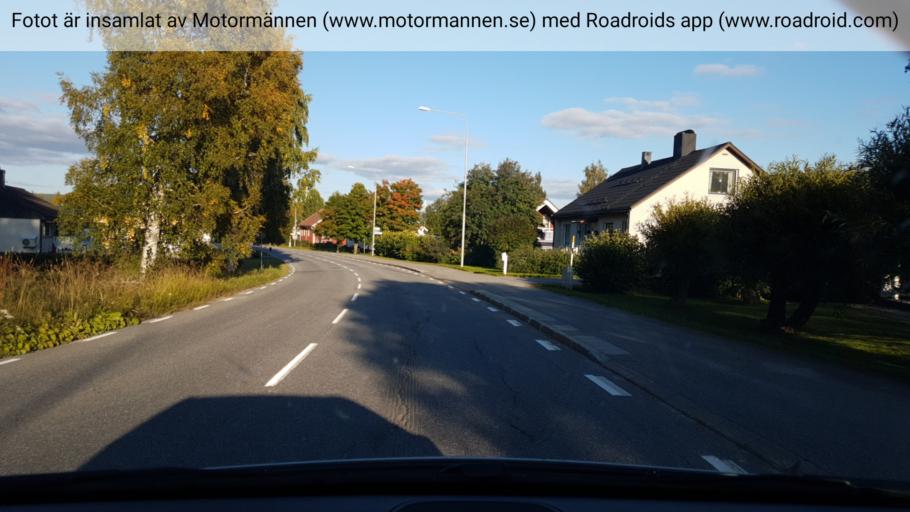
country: SE
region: Vaesterbotten
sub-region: Vannas Kommun
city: Vannasby
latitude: 63.9123
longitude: 19.8248
